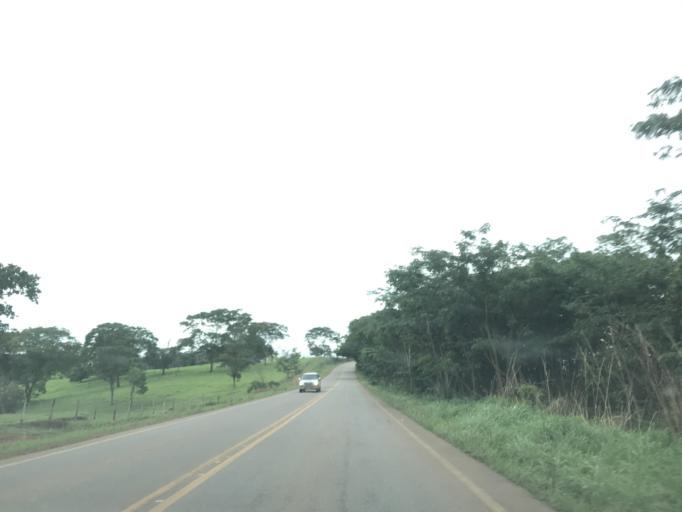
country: BR
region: Goias
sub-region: Vianopolis
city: Vianopolis
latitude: -16.7118
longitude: -48.4016
